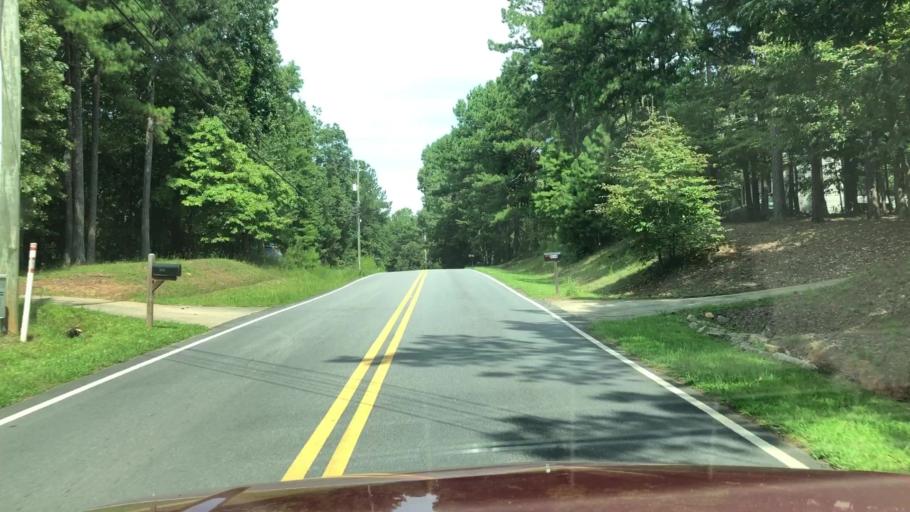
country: US
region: Georgia
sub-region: Cherokee County
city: Woodstock
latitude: 34.1514
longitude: -84.5948
